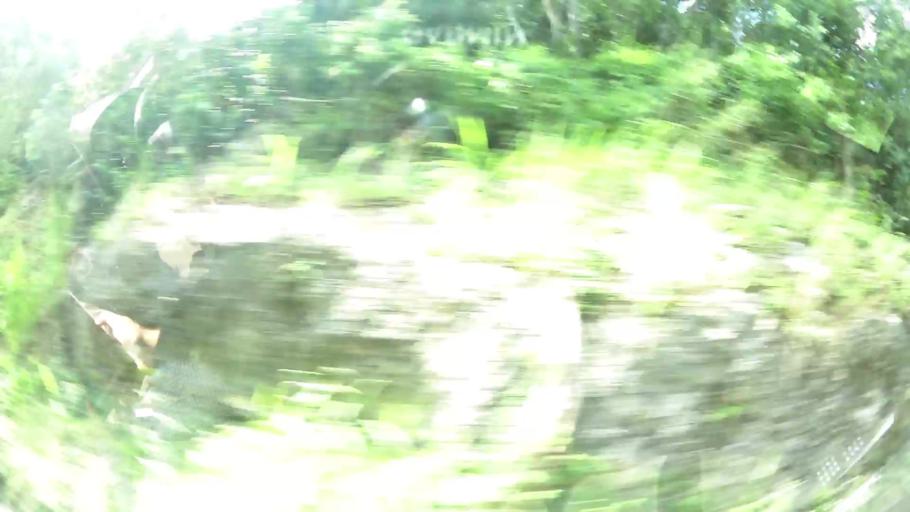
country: GP
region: Guadeloupe
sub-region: Guadeloupe
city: Anse-Bertrand
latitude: 16.4360
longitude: -61.4756
